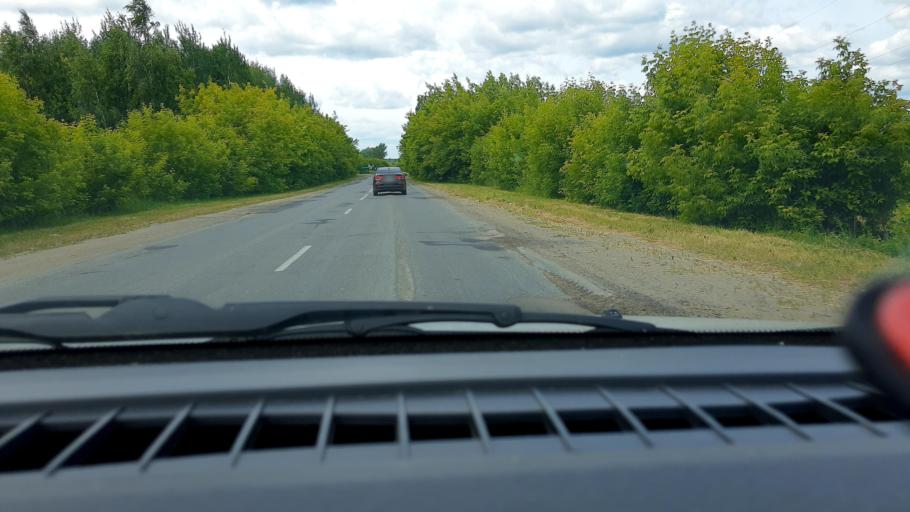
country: RU
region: Nizjnij Novgorod
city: Kstovo
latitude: 56.1323
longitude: 44.1006
